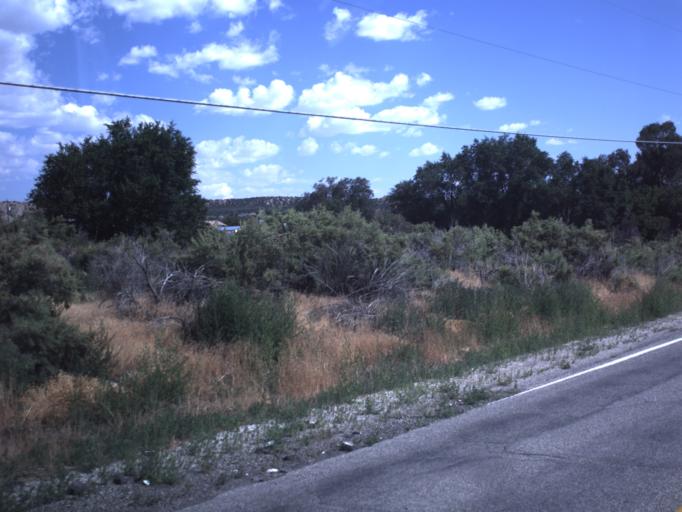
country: US
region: Utah
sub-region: Carbon County
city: Spring Glen
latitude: 39.6581
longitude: -110.8562
